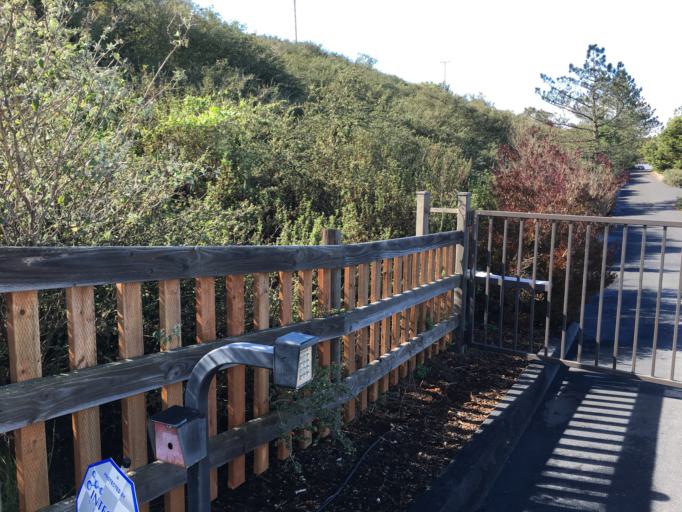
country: US
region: California
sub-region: San Luis Obispo County
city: Avila Beach
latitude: 35.2545
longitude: -120.7617
